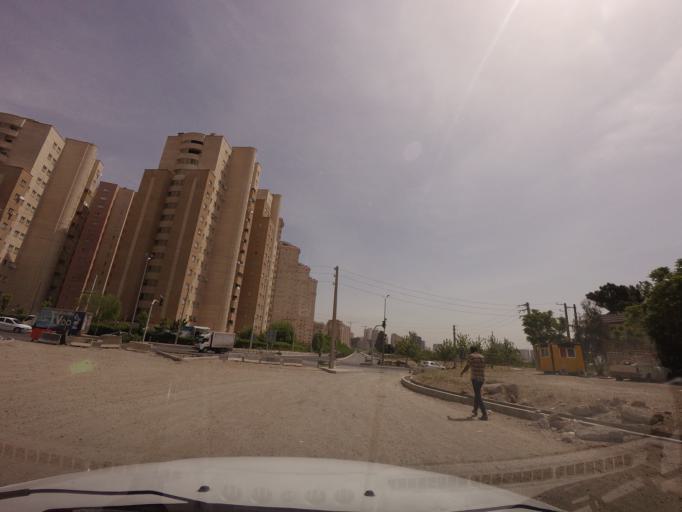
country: IR
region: Tehran
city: Shahr-e Qods
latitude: 35.7527
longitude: 51.1976
